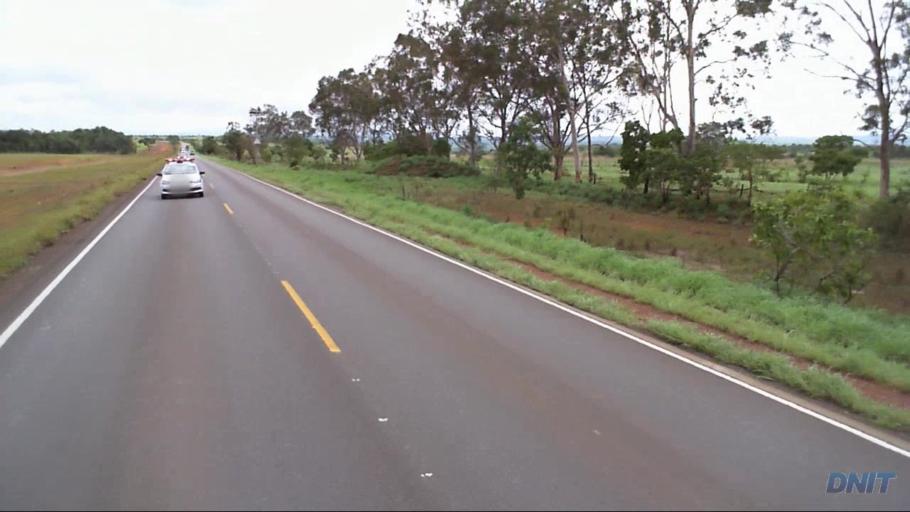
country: BR
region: Goias
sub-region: Padre Bernardo
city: Padre Bernardo
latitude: -15.3184
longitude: -48.2292
